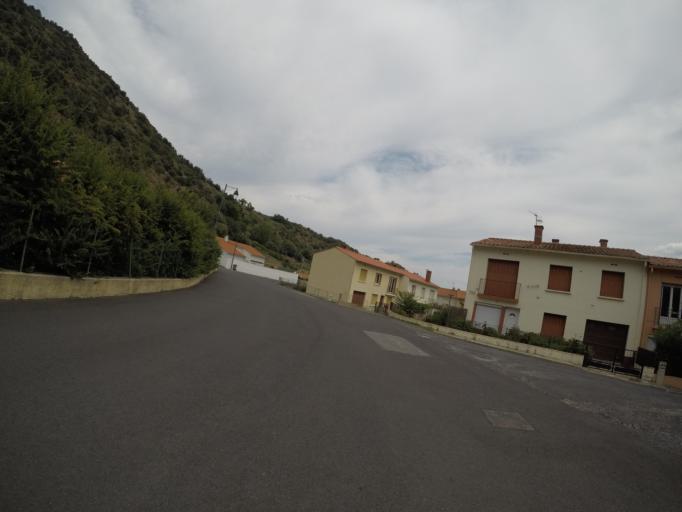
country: FR
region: Languedoc-Roussillon
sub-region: Departement des Pyrenees-Orientales
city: Ria-Sirach
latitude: 42.6065
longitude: 2.3907
